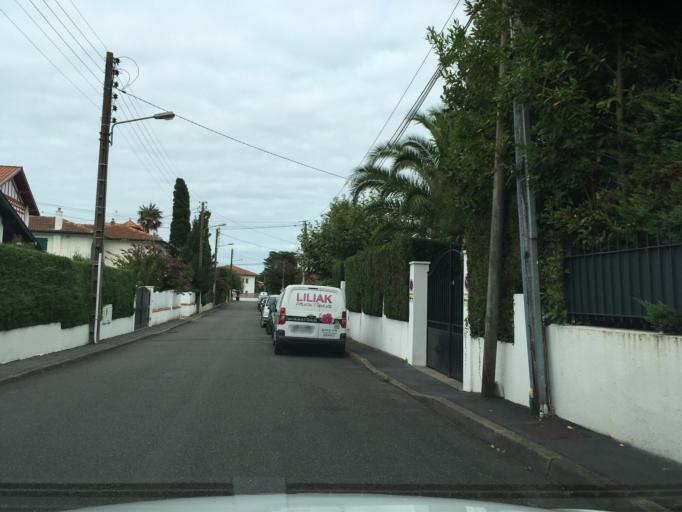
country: FR
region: Aquitaine
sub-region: Departement des Pyrenees-Atlantiques
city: Biarritz
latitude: 43.4776
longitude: -1.5365
